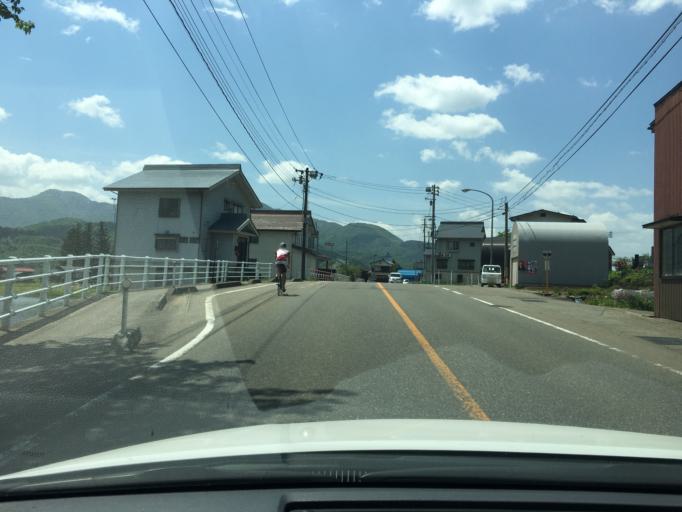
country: JP
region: Niigata
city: Tochio-honcho
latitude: 37.3294
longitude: 139.0265
